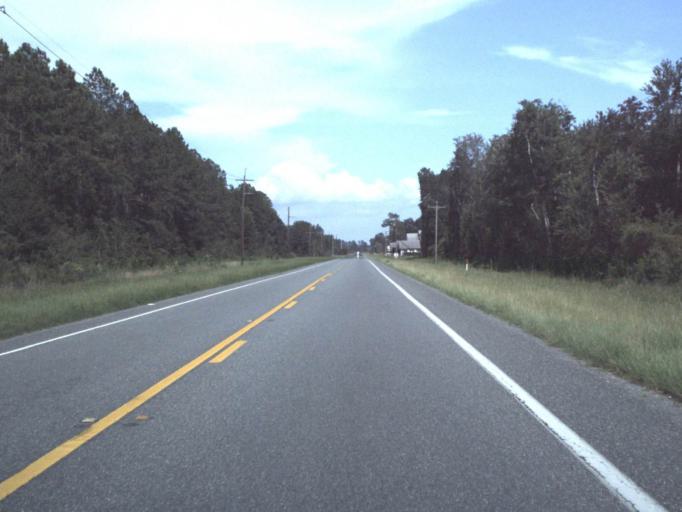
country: US
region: Florida
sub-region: Bradford County
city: Starke
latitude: 29.9619
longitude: -82.1733
